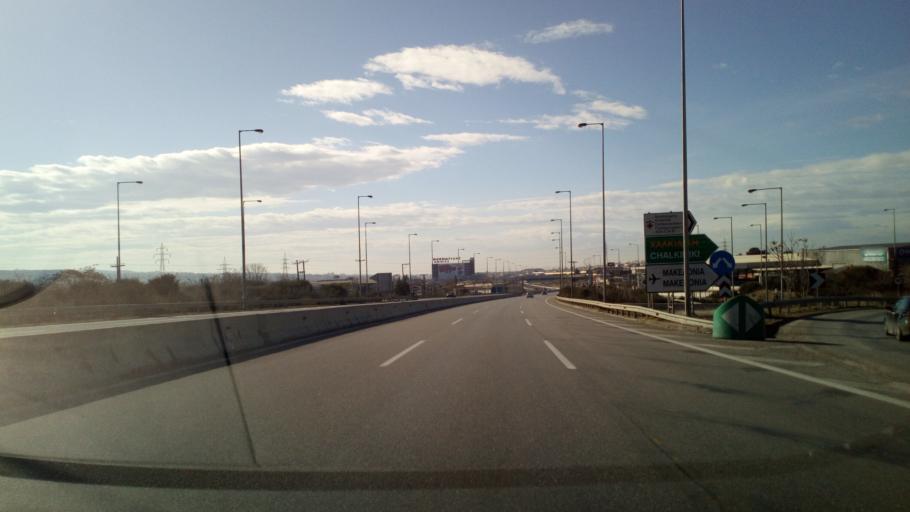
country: GR
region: Central Macedonia
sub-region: Nomos Thessalonikis
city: Efkarpia
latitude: 40.6950
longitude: 22.9473
